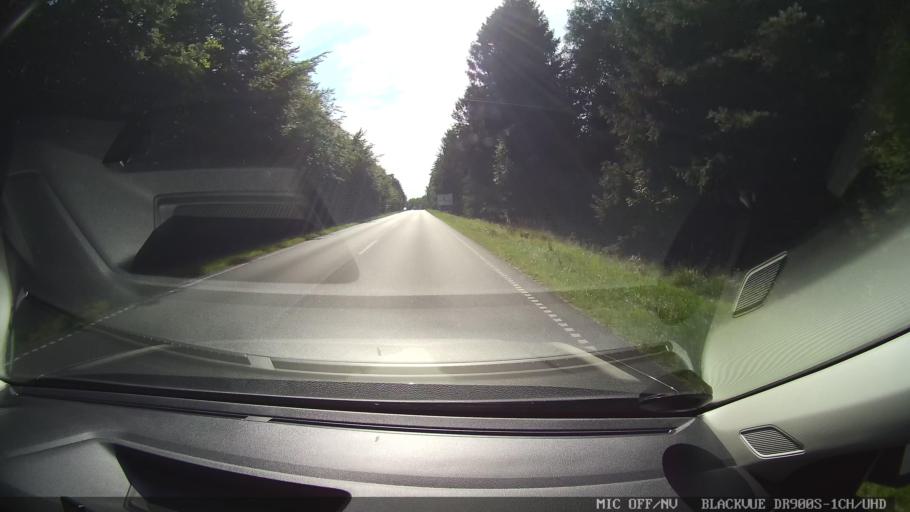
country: DK
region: North Denmark
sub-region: Mariagerfjord Kommune
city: Hadsund
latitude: 56.7265
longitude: 10.0906
